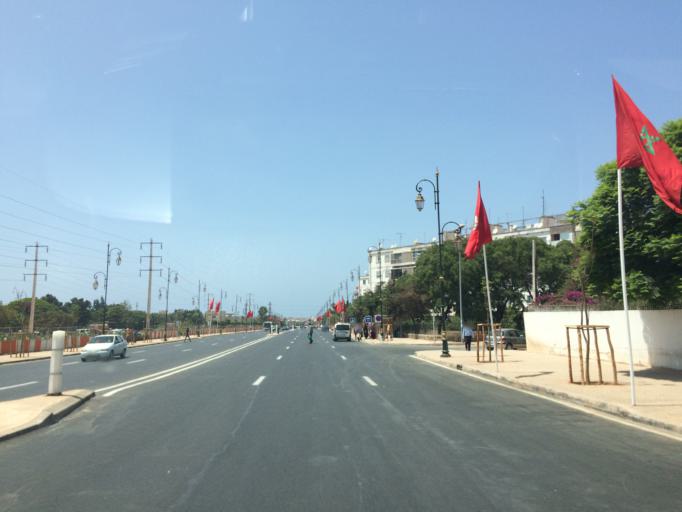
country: MA
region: Rabat-Sale-Zemmour-Zaer
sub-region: Rabat
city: Rabat
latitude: 33.9878
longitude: -6.8533
